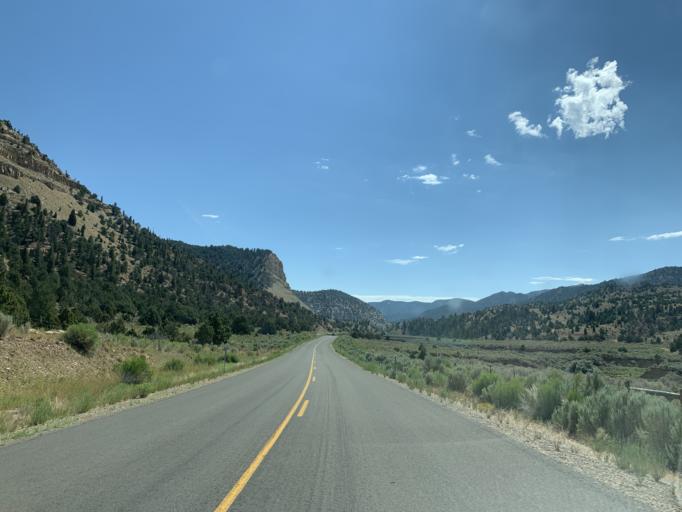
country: US
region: Utah
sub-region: Carbon County
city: East Carbon City
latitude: 39.7760
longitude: -110.4906
